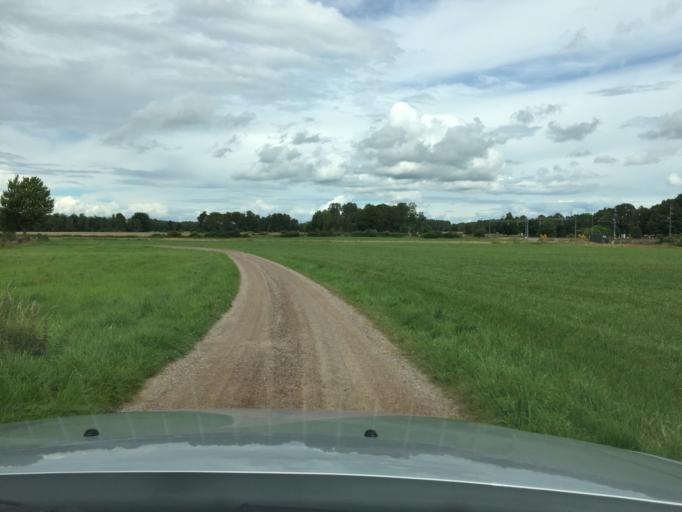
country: SE
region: Skane
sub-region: Hassleholms Kommun
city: Sosdala
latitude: 56.0173
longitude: 13.6500
